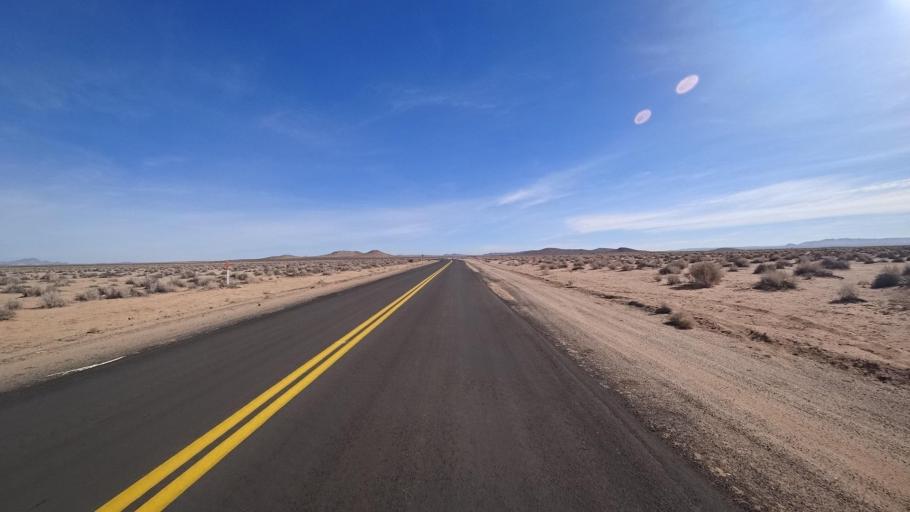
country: US
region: California
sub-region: Kern County
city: North Edwards
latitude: 35.0728
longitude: -117.7982
